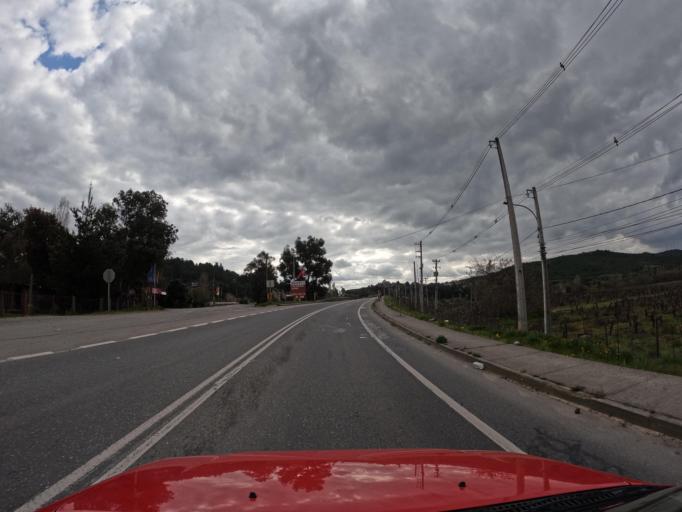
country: CL
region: Maule
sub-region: Provincia de Linares
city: San Javier
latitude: -35.6217
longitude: -71.7660
